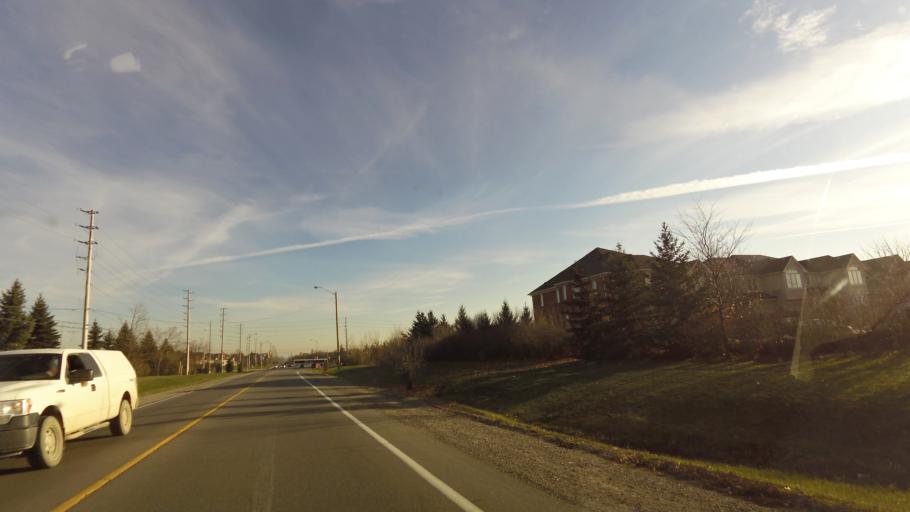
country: CA
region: Ontario
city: Brampton
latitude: 43.7742
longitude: -79.7129
